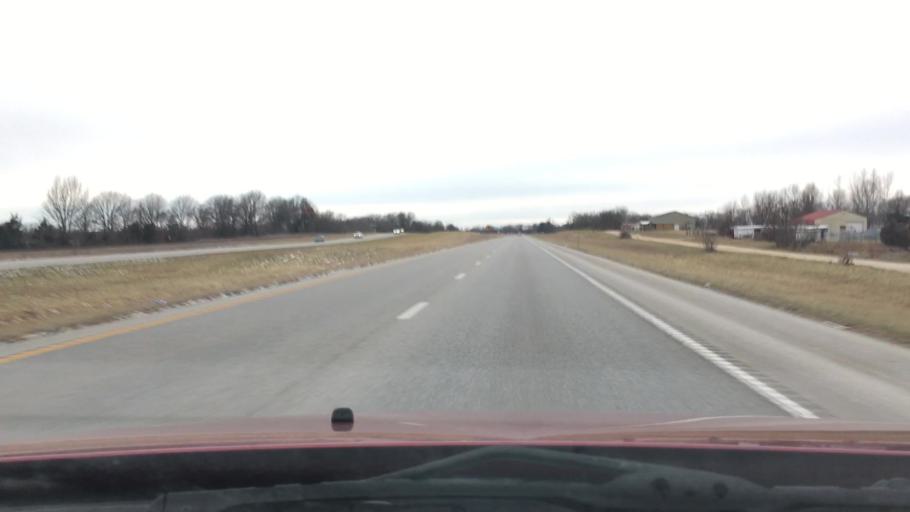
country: US
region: Missouri
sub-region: Webster County
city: Seymour
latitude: 37.1600
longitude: -92.7927
